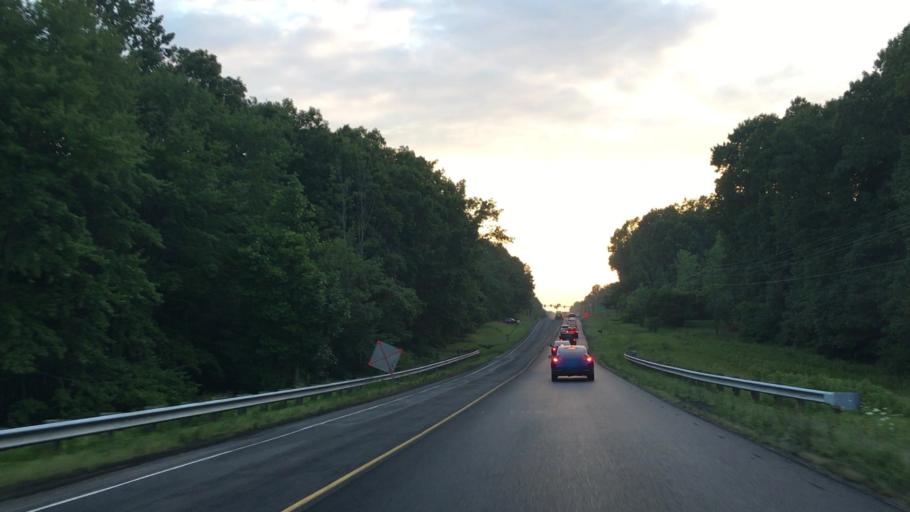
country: US
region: Virginia
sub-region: Spotsylvania County
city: Spotsylvania
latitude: 38.3130
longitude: -77.7745
